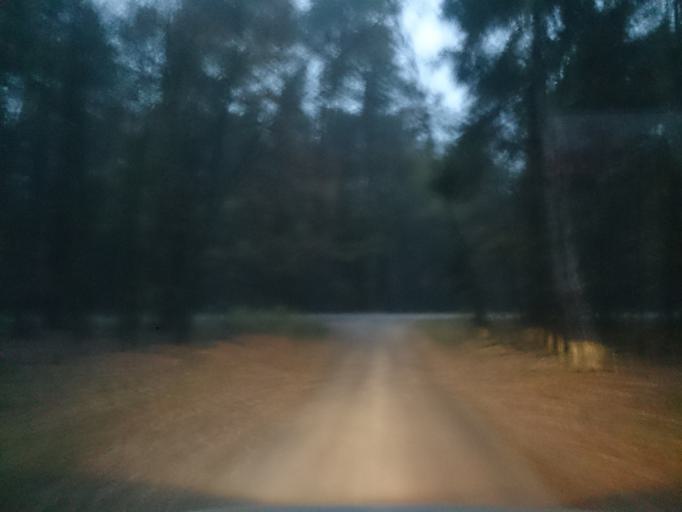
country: PL
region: Kujawsko-Pomorskie
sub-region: Powiat wabrzeski
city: Debowa Laka
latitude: 53.1892
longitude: 19.1532
